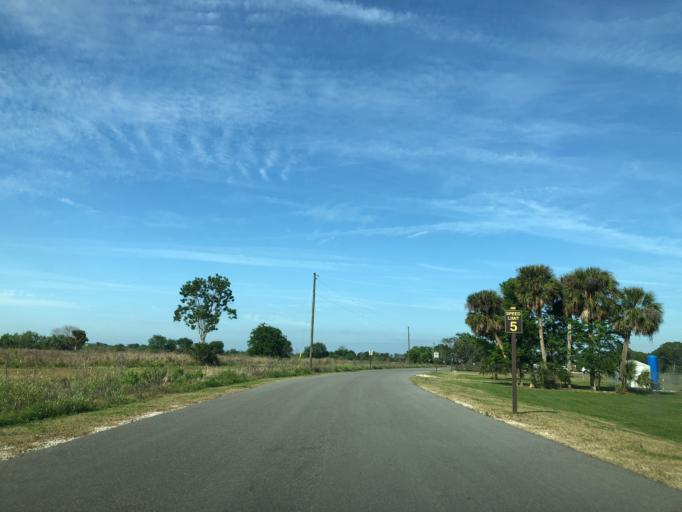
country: US
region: Florida
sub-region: Lake County
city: Astatula
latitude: 28.7044
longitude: -81.6740
